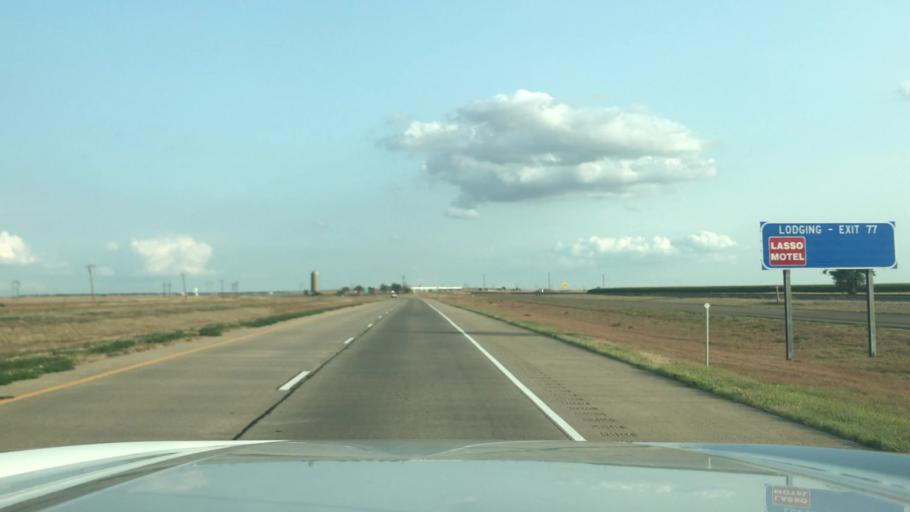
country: US
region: Texas
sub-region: Swisher County
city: Tulia
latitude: 34.5924
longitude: -101.8016
